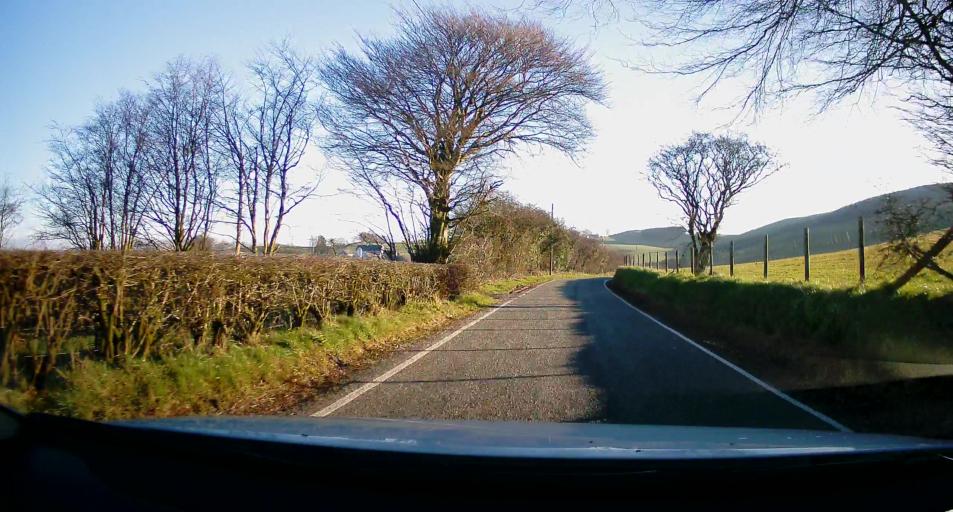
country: GB
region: Wales
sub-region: County of Ceredigion
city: Lledrod
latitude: 52.2677
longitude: -4.0699
